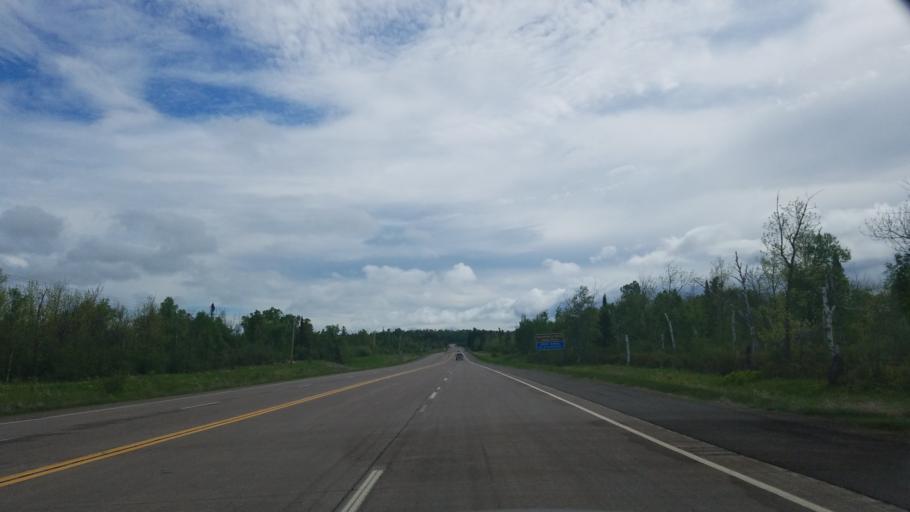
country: US
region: Minnesota
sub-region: Lake County
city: Two Harbors
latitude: 47.1335
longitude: -91.4821
